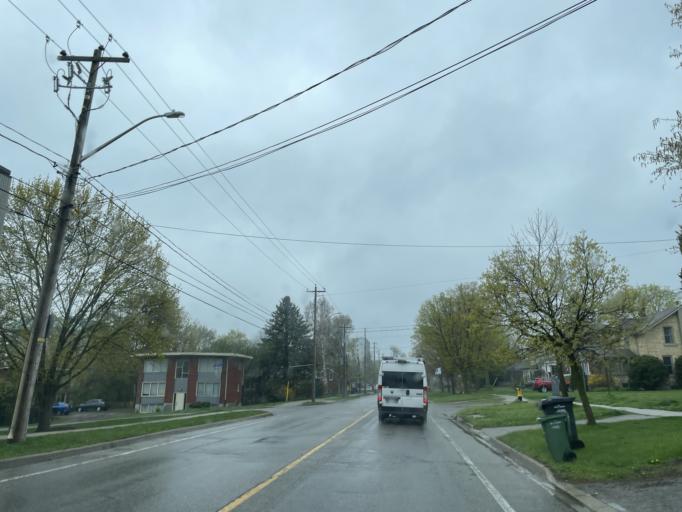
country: CA
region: Ontario
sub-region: Wellington County
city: Guelph
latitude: 43.5341
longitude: -80.2577
